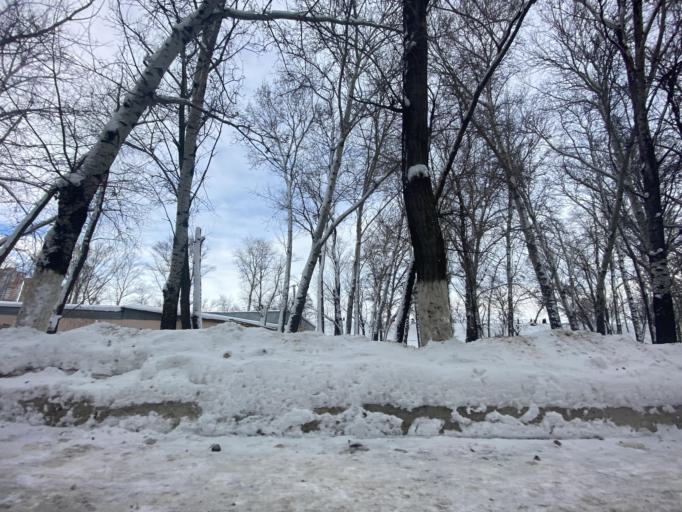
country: RU
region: Saratov
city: Engel's
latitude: 51.5014
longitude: 46.1029
